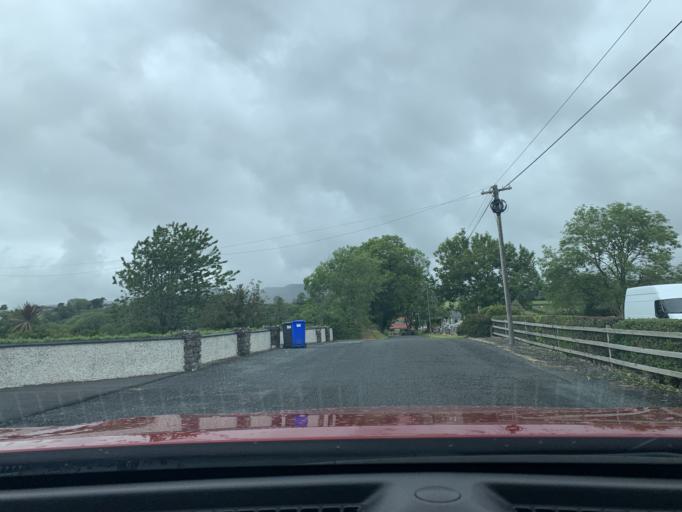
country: IE
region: Connaught
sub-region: Sligo
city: Sligo
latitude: 54.3007
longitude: -8.4581
